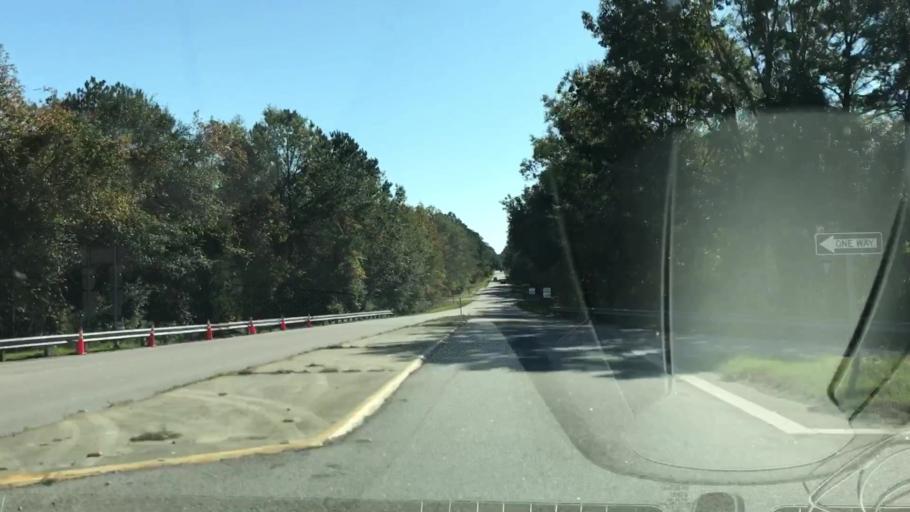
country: US
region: South Carolina
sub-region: Jasper County
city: Ridgeland
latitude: 32.5784
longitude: -80.9294
